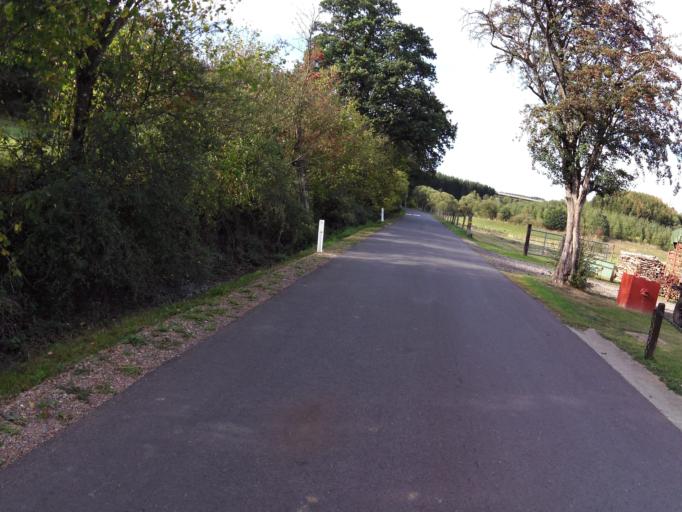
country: BE
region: Wallonia
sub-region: Province de Liege
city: Saint-Vith
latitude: 50.2563
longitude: 6.1461
